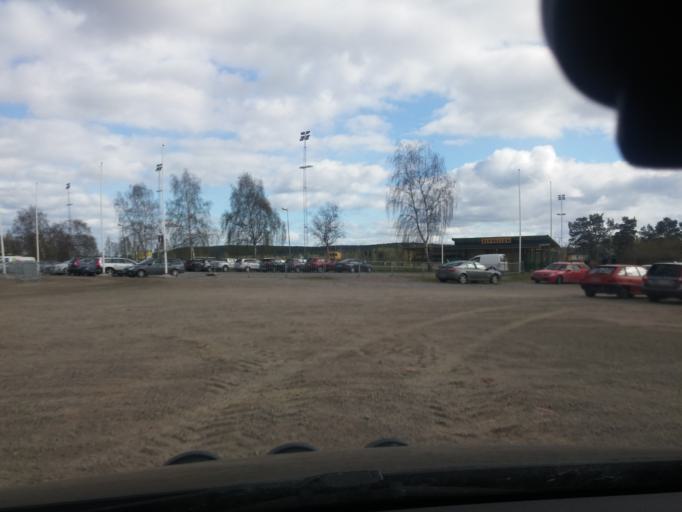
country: SE
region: Gaevleborg
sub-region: Ljusdals Kommun
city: Ljusdal
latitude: 61.8199
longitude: 16.0819
